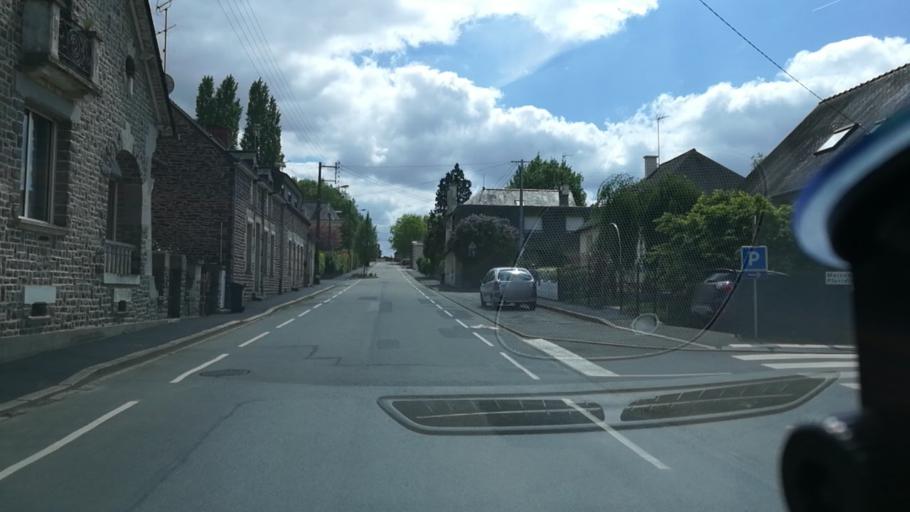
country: FR
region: Brittany
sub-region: Departement d'Ille-et-Vilaine
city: Retiers
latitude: 47.9108
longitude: -1.3794
